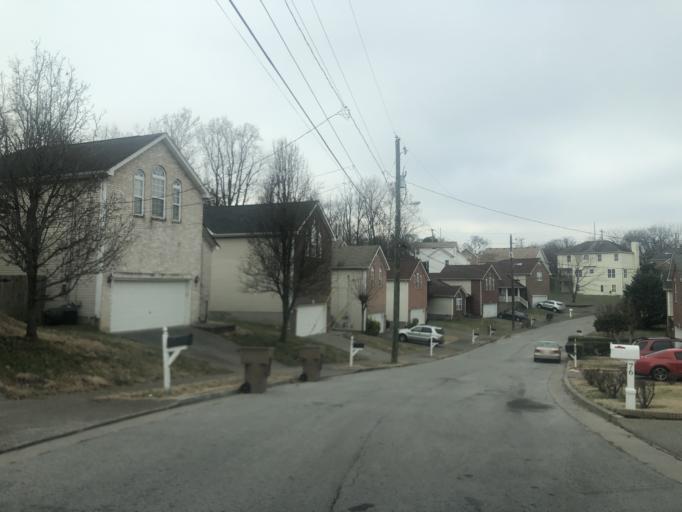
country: US
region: Tennessee
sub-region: Rutherford County
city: La Vergne
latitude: 36.0823
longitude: -86.6431
